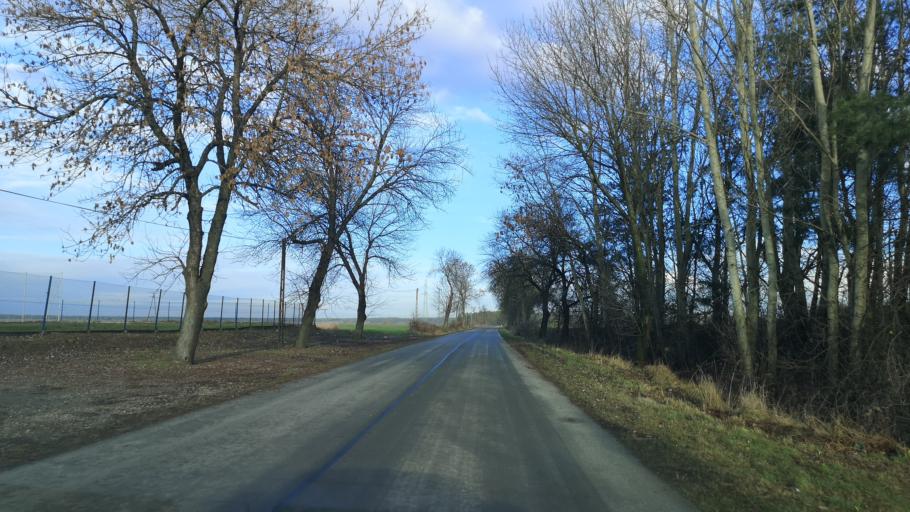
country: PL
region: Subcarpathian Voivodeship
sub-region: Powiat lezajski
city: Piskorowice
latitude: 50.2367
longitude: 22.5317
